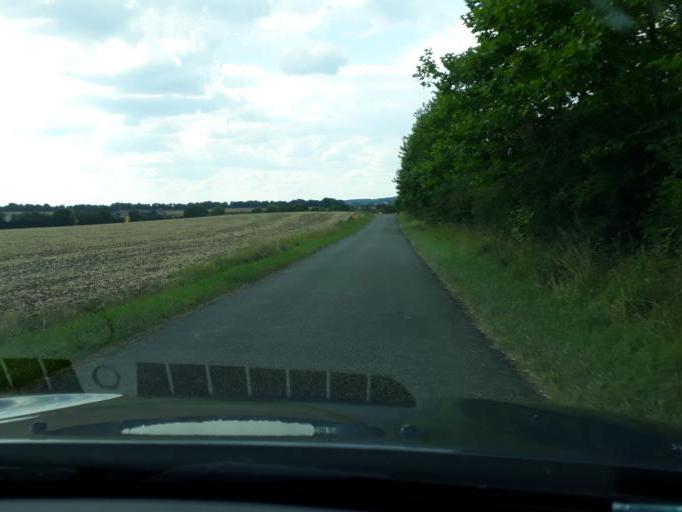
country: FR
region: Centre
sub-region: Departement du Cher
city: Jouet-sur-l'Aubois
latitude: 46.9824
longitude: 2.9308
